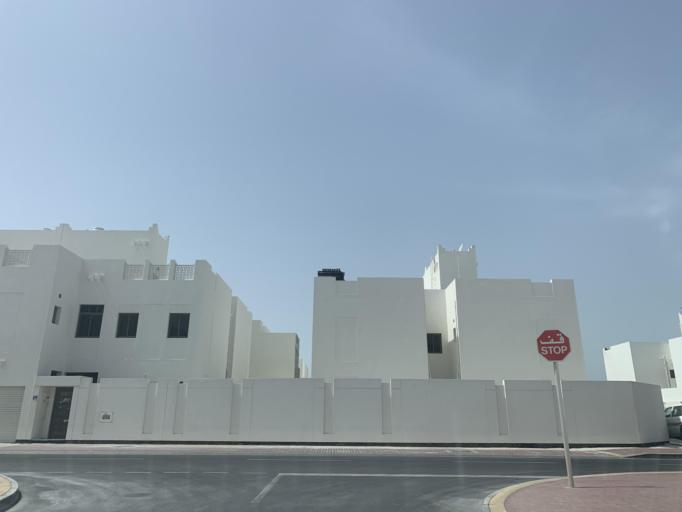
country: BH
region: Northern
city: Ar Rifa'
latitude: 26.1516
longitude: 50.5628
